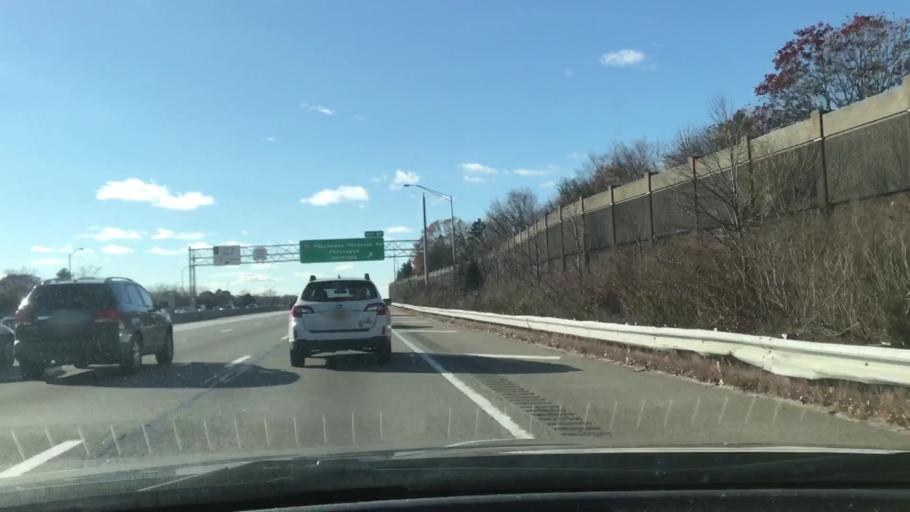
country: US
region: New York
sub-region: Suffolk County
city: Holbrook
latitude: 40.8169
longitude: -73.0768
